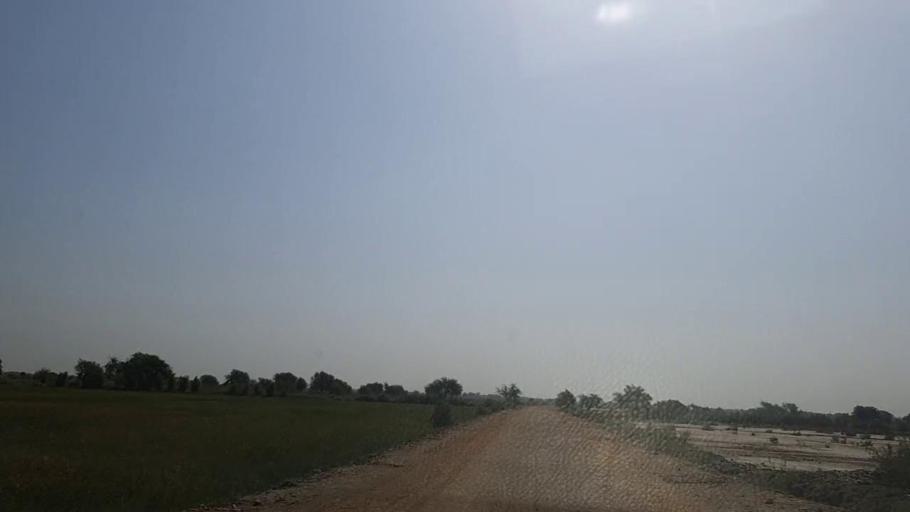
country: PK
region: Sindh
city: Daro Mehar
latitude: 24.7077
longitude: 68.1254
